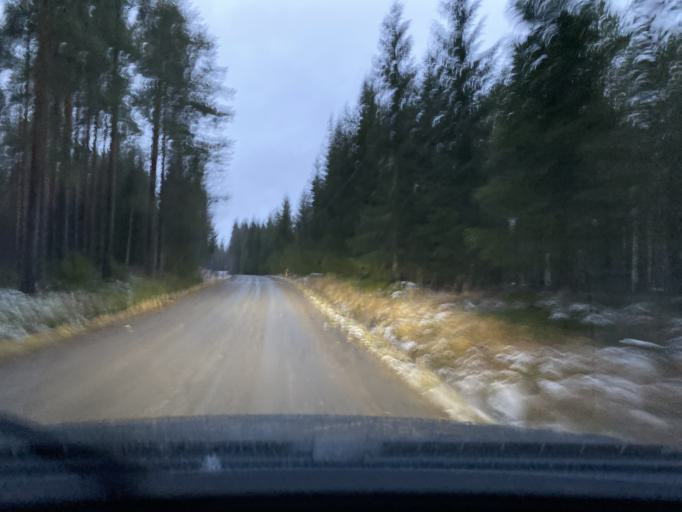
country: FI
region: Pirkanmaa
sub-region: Lounais-Pirkanmaa
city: Punkalaidun
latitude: 61.1477
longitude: 22.9506
